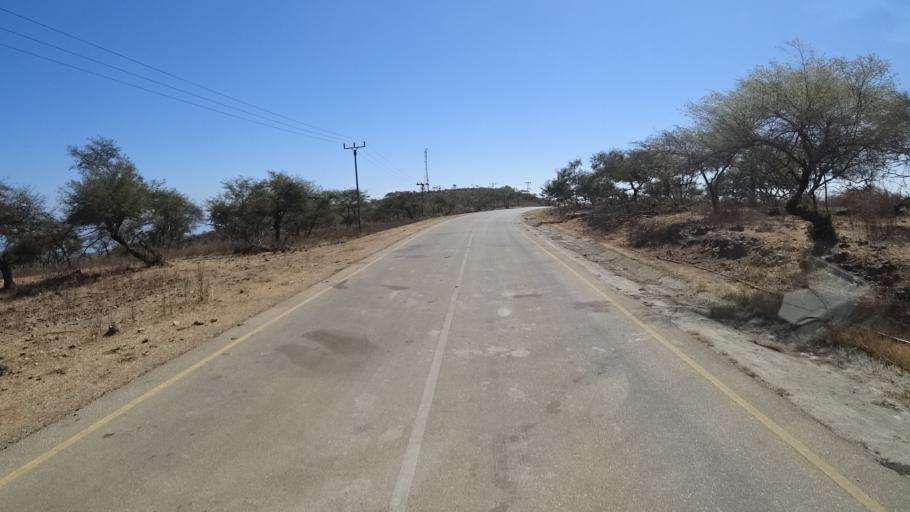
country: YE
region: Al Mahrah
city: Hawf
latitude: 16.7754
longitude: 53.3366
